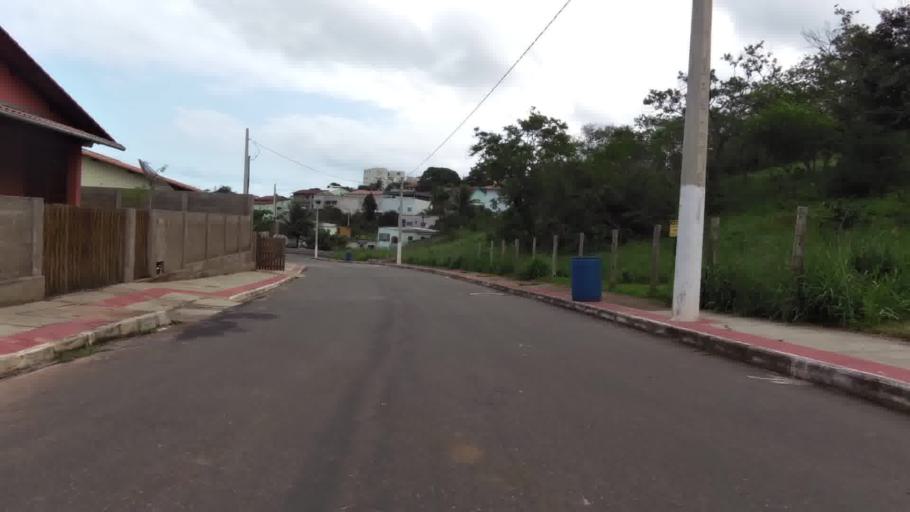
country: BR
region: Espirito Santo
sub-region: Piuma
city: Piuma
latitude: -20.8016
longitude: -40.6487
